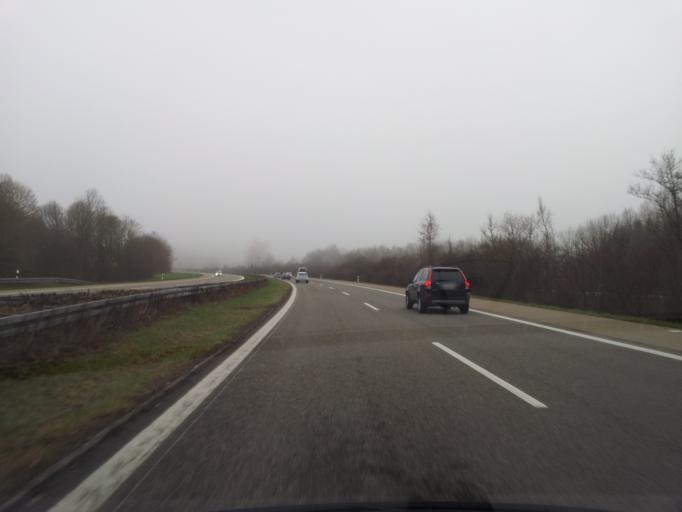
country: DE
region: Baden-Wuerttemberg
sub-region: Freiburg Region
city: Volkertshausen
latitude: 47.8104
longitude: 8.8545
